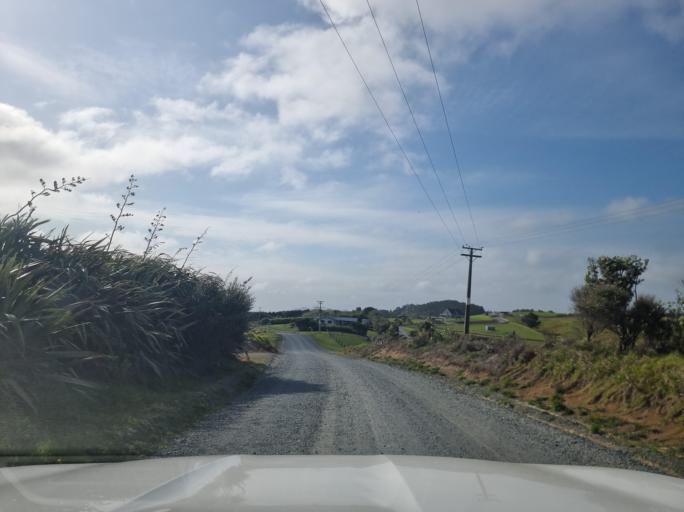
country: NZ
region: Northland
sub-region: Whangarei
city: Ruakaka
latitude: -36.0134
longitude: 174.4779
